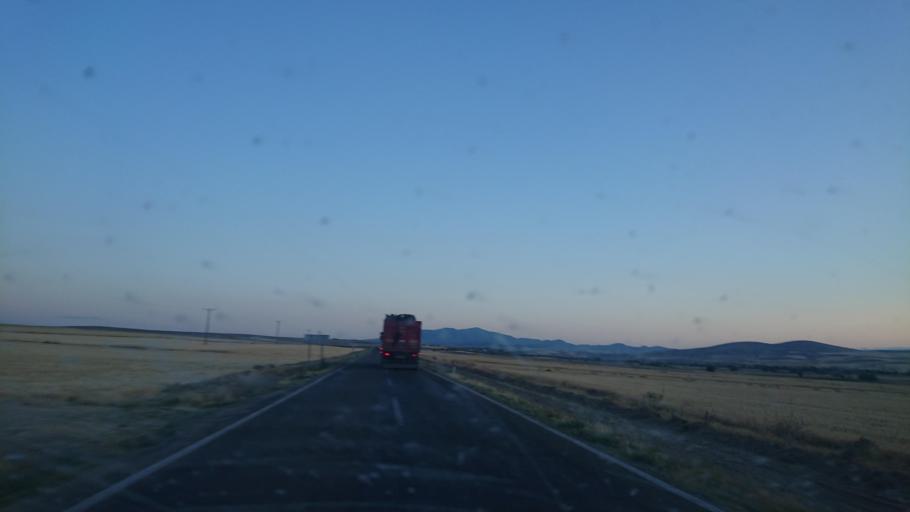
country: TR
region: Aksaray
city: Balci
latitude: 38.8219
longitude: 34.1358
